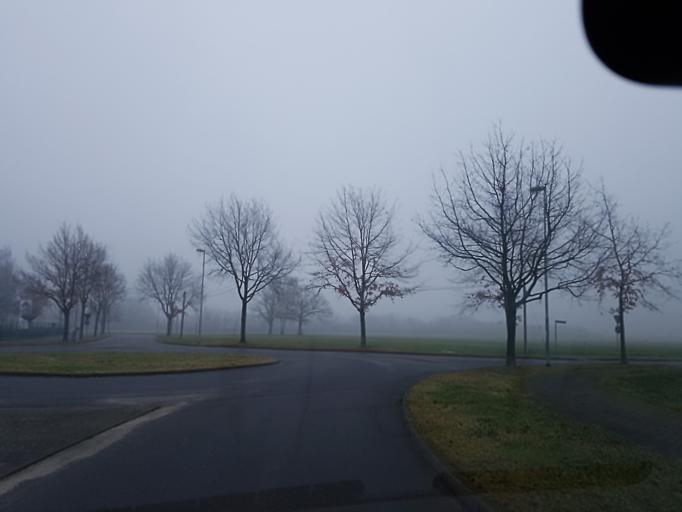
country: DE
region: Brandenburg
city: Finsterwalde
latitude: 51.6316
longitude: 13.7372
